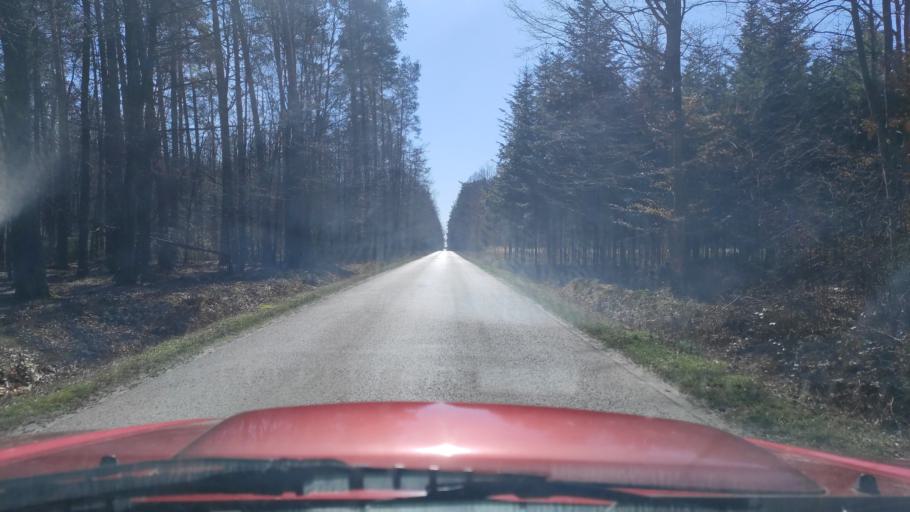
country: PL
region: Masovian Voivodeship
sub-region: Powiat radomski
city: Pionki
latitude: 51.5048
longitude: 21.4682
